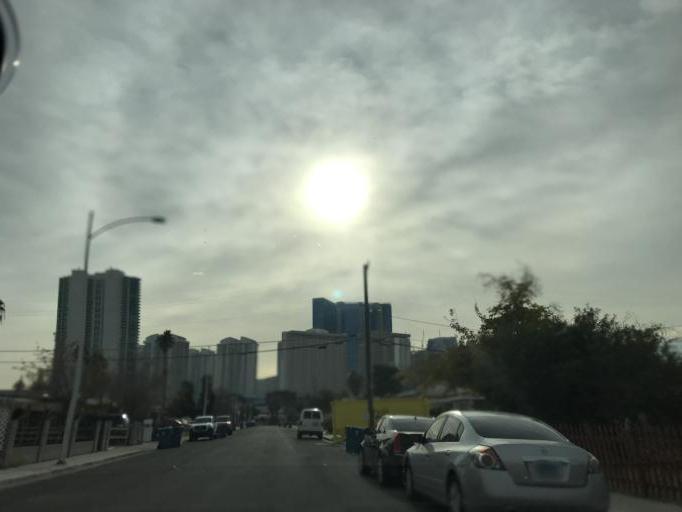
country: US
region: Nevada
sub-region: Clark County
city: Las Vegas
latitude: 36.1460
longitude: -115.1526
